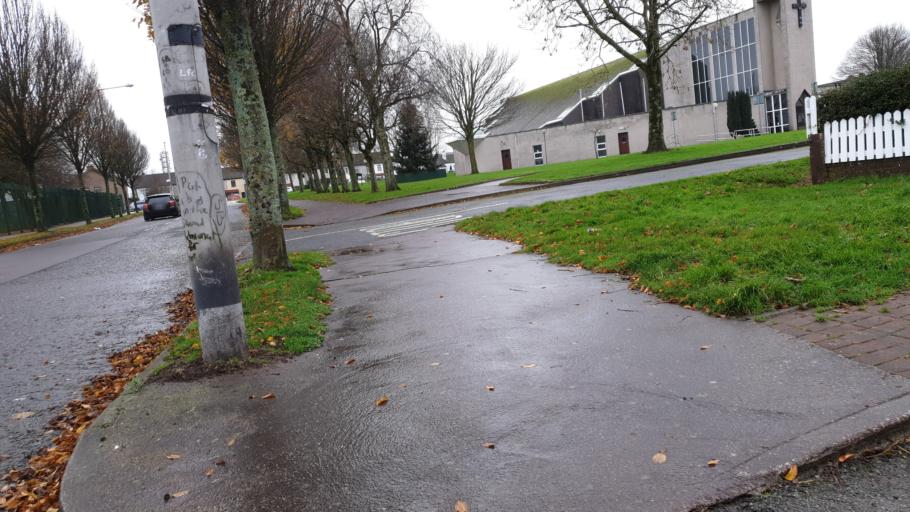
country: IE
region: Munster
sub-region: County Cork
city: Passage West
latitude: 51.8918
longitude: -8.4042
